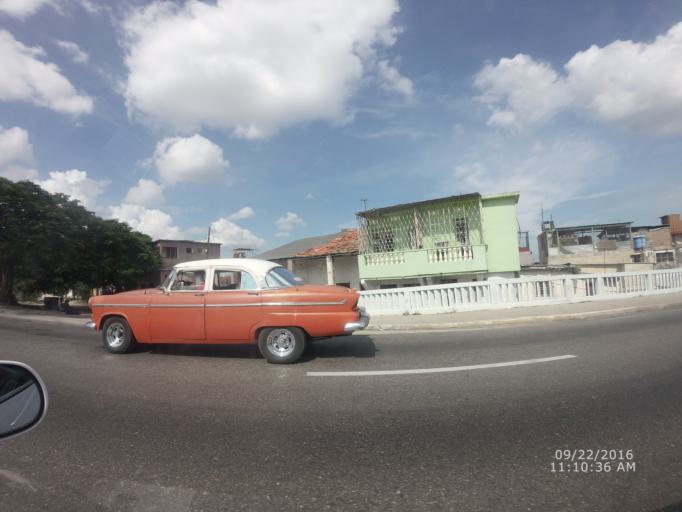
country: CU
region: La Habana
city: Cerro
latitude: 23.1003
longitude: -82.4207
